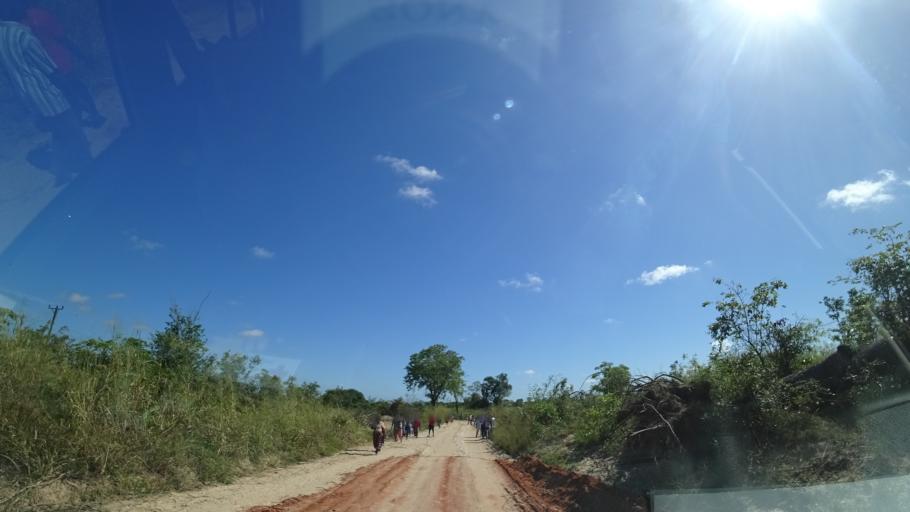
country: MZ
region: Sofala
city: Dondo
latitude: -19.2775
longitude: 34.6820
